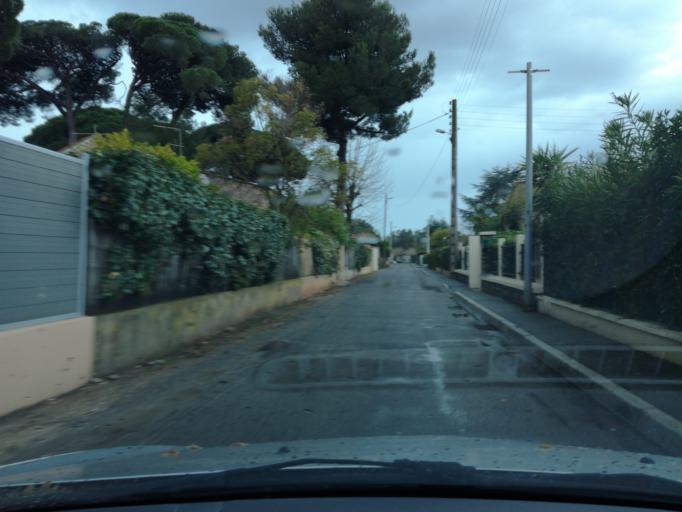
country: FR
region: Provence-Alpes-Cote d'Azur
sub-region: Departement du Var
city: Hyeres
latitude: 43.1036
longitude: 6.1728
